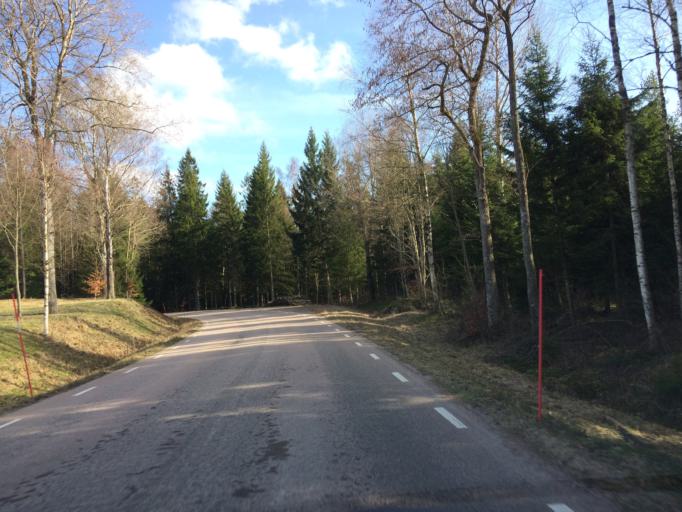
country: SE
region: Kronoberg
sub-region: Ljungby Kommun
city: Ljungby
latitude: 56.6423
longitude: 13.9469
